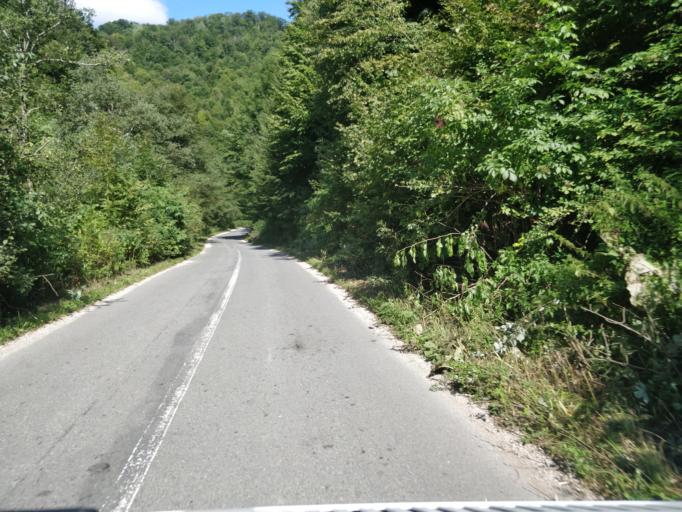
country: RO
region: Cluj
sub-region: Comuna Sacueu
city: Sacuieu
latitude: 46.8415
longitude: 22.8621
